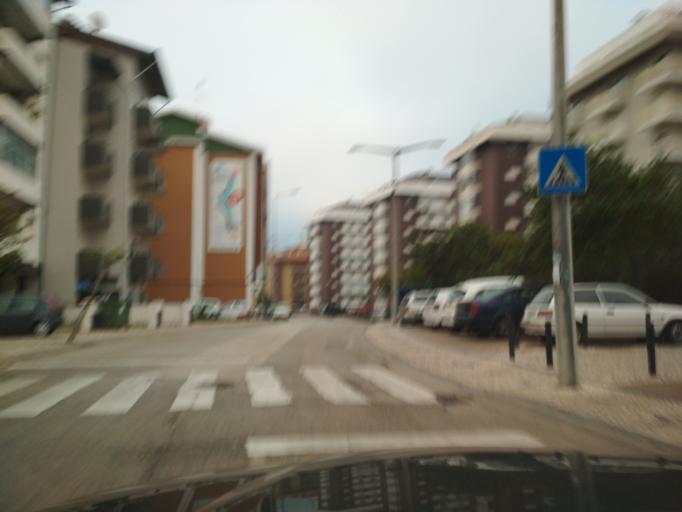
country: PT
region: Coimbra
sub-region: Coimbra
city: Coimbra
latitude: 40.1971
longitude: -8.4074
